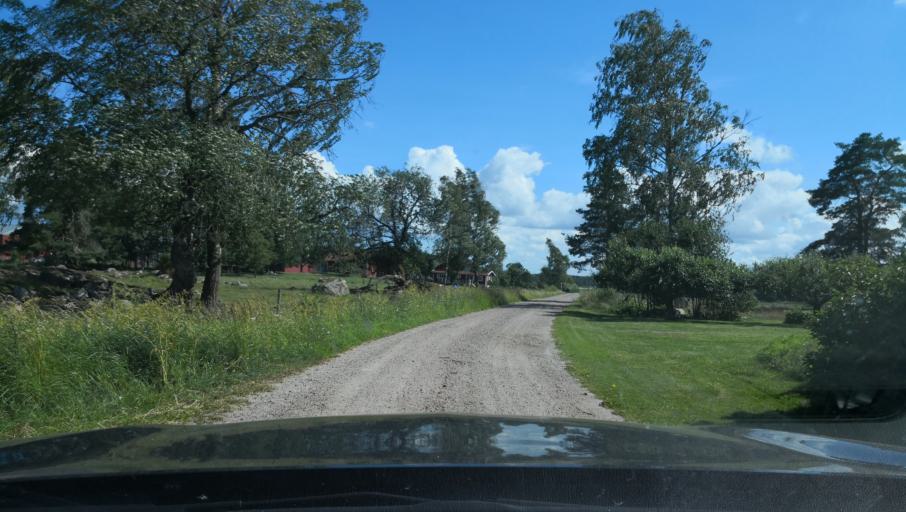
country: SE
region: Vaestmanland
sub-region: Kungsors Kommun
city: Kungsoer
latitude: 59.3233
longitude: 16.0572
